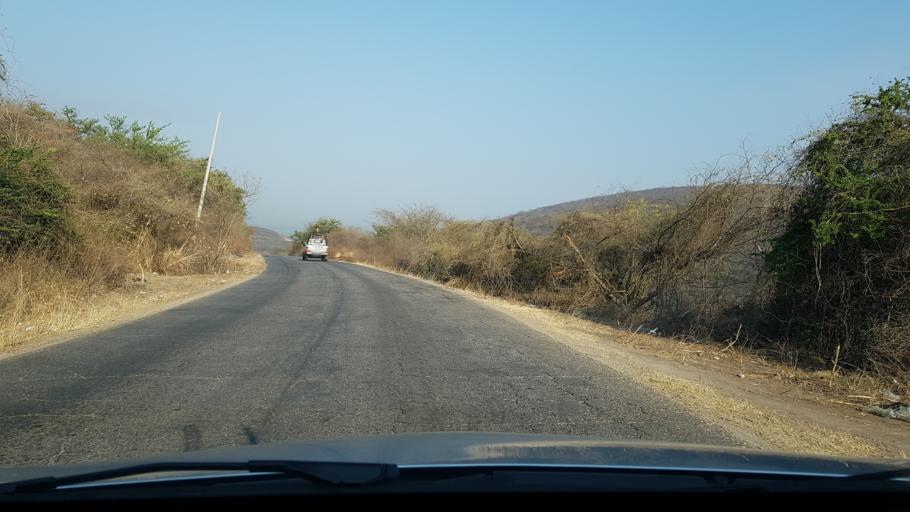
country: MX
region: Morelos
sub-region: Tlaltizapan de Zapata
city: Colonia Palo Prieto (Chipitongo)
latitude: 18.6751
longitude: -99.0619
